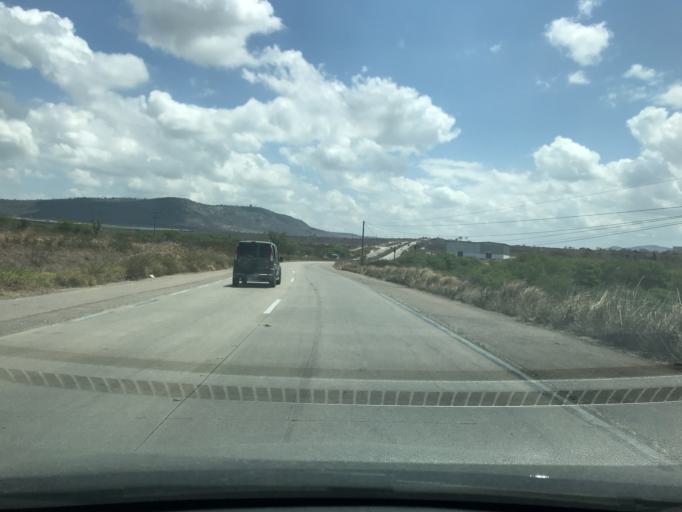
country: BR
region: Pernambuco
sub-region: Bezerros
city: Bezerros
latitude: -8.2885
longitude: -35.8203
